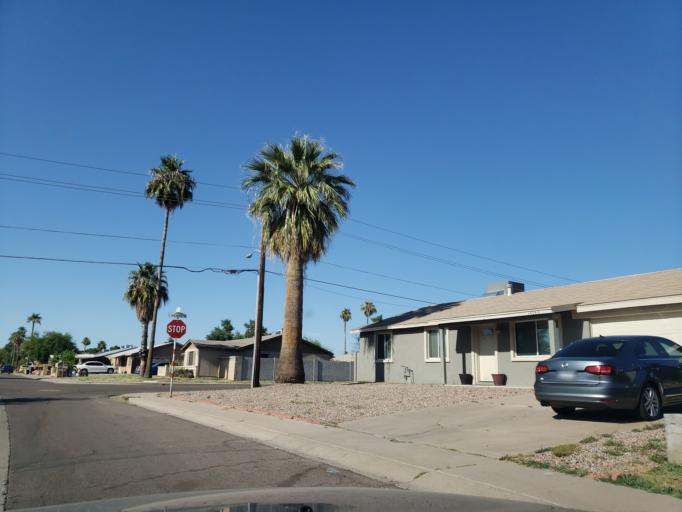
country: US
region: Arizona
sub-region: Maricopa County
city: Paradise Valley
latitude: 33.6151
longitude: -112.0003
